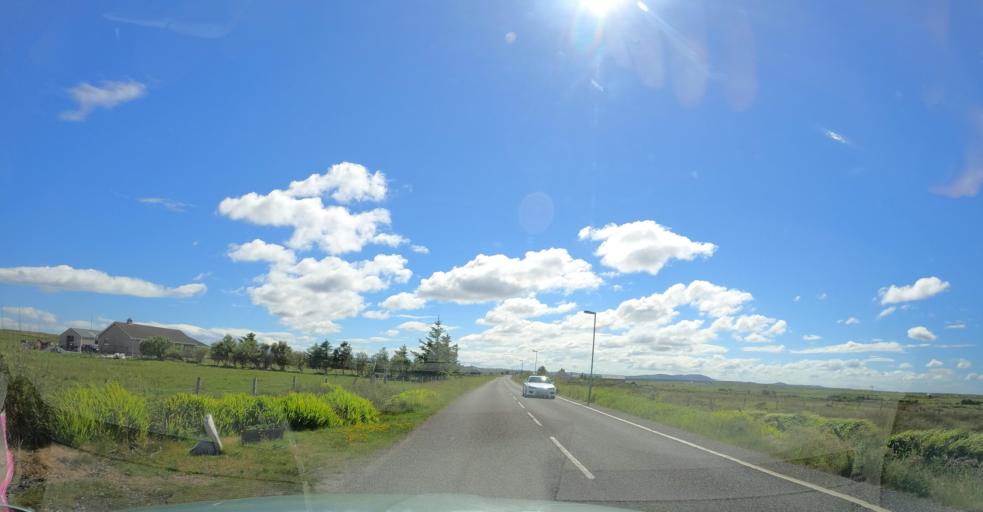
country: GB
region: Scotland
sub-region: Eilean Siar
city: Isle of Lewis
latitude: 58.3636
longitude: -6.5085
